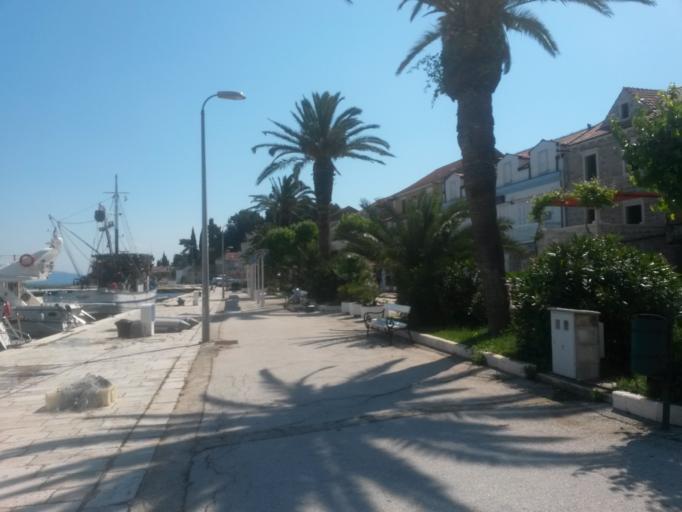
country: HR
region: Dubrovacko-Neretvanska
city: Orebic
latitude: 43.0090
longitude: 17.2655
